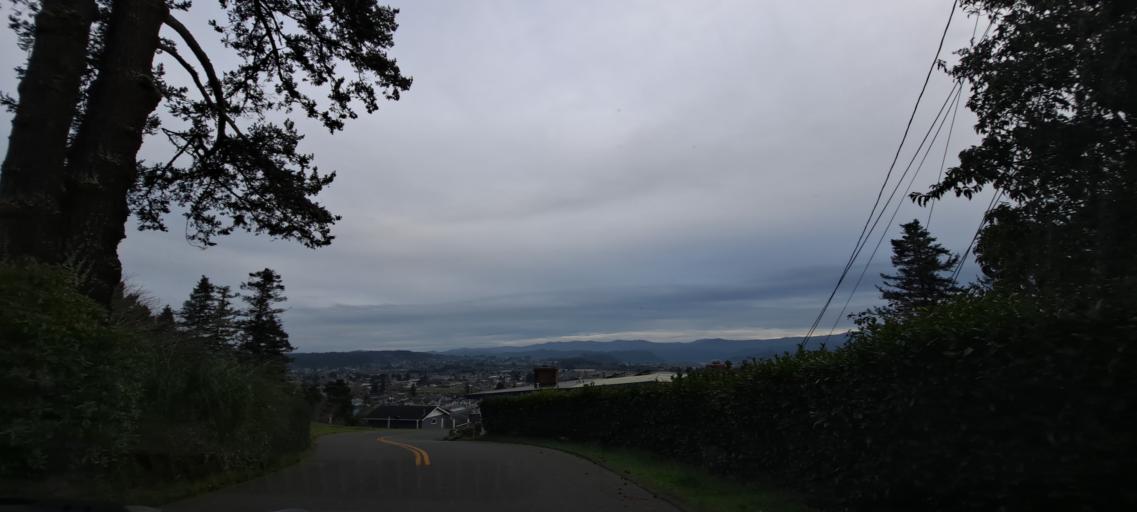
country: US
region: California
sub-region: Humboldt County
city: Fortuna
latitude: 40.6019
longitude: -124.1542
